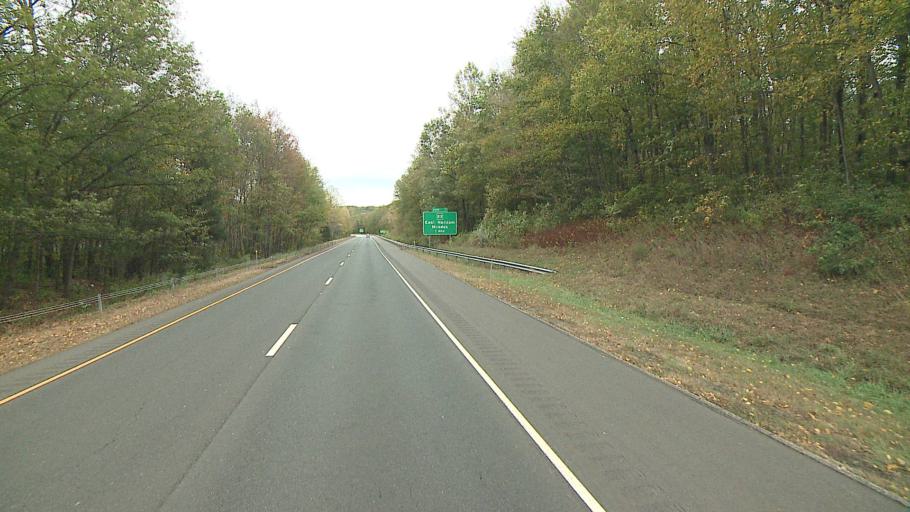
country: US
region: Connecticut
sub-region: Middlesex County
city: East Haddam
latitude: 41.4286
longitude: -72.5082
